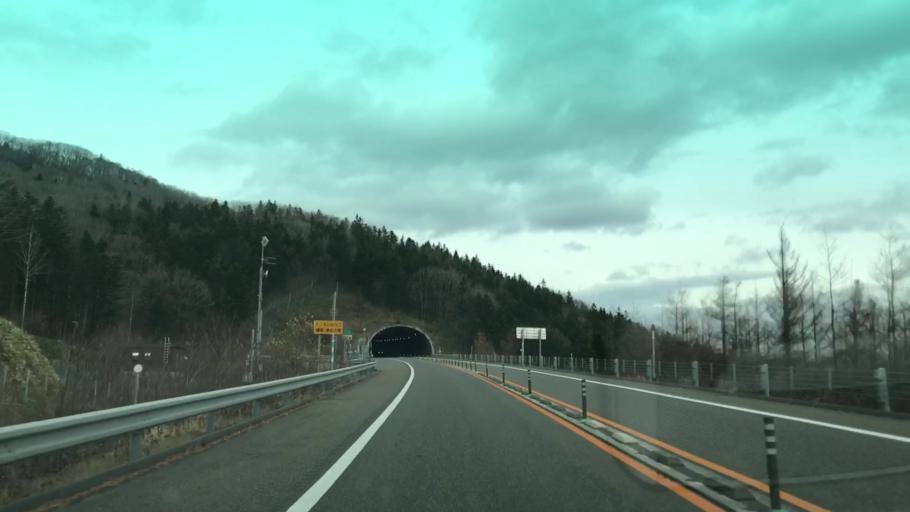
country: JP
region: Hokkaido
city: Otofuke
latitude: 43.0511
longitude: 142.7845
